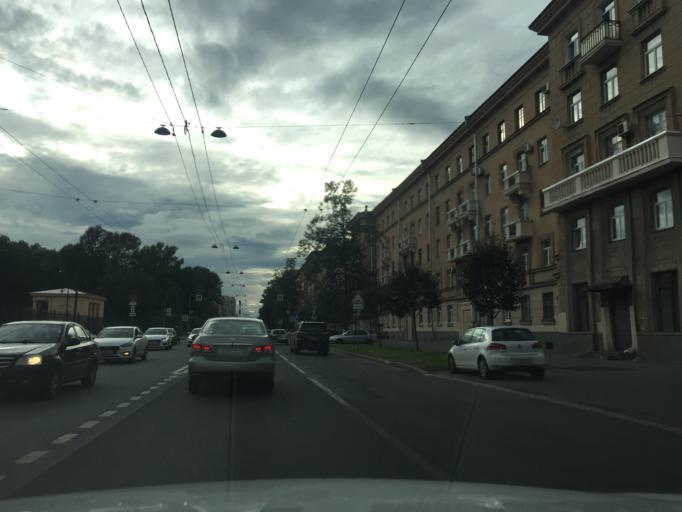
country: RU
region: St.-Petersburg
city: Kupchino
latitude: 59.8718
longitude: 30.3268
